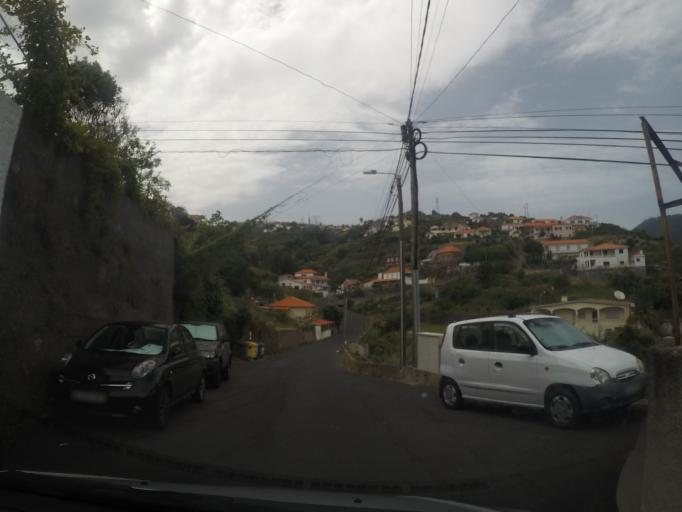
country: PT
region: Madeira
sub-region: Santa Cruz
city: Santa Cruz
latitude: 32.6864
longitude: -16.8080
